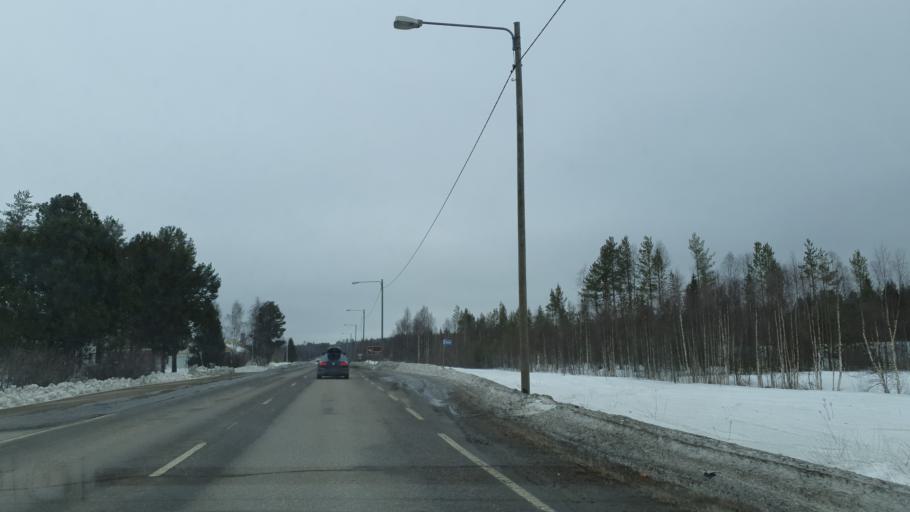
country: FI
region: Lapland
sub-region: Torniolaakso
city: Pello
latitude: 66.8164
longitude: 24.0013
